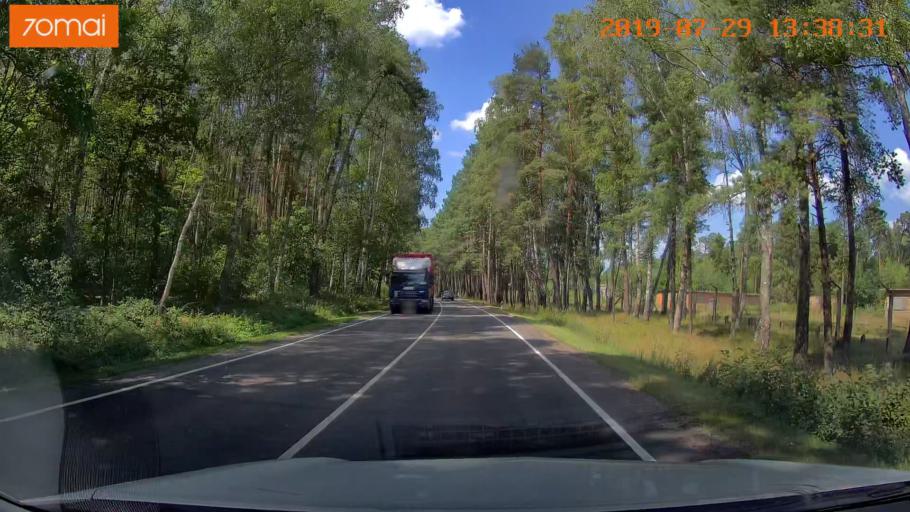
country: RU
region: Kaliningrad
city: Volochayevskoye
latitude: 54.7216
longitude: 20.1698
